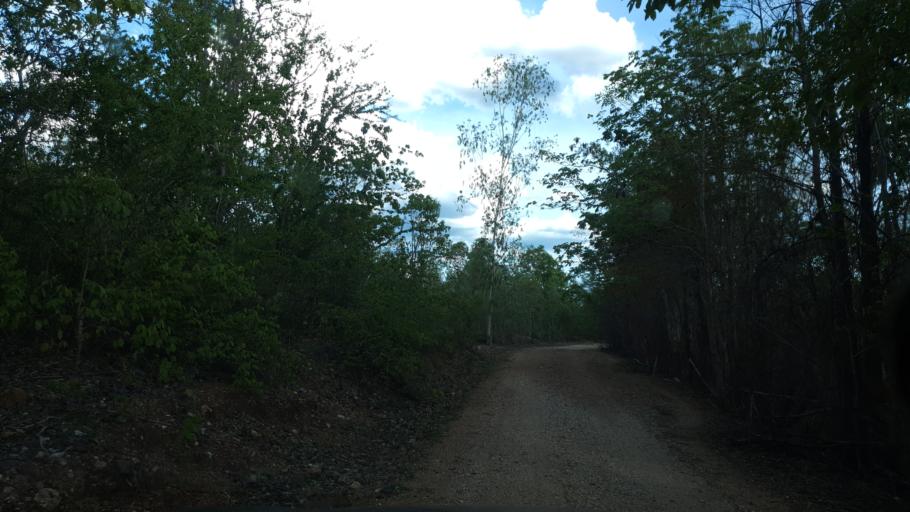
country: TH
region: Lampang
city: Sop Prap
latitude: 17.8839
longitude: 99.2926
